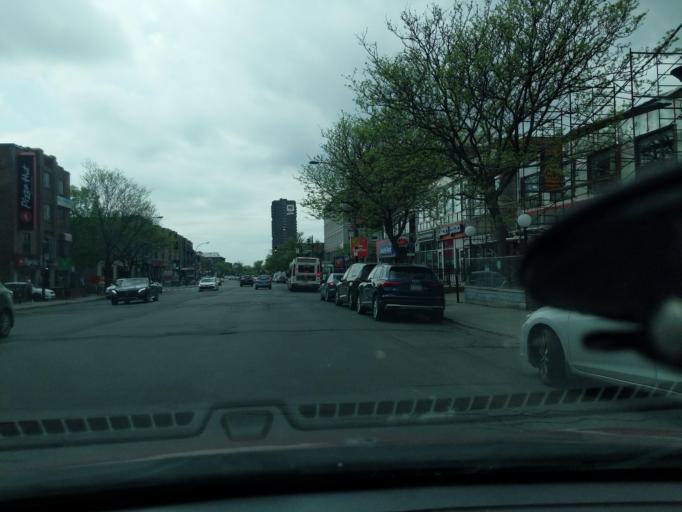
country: CA
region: Quebec
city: Saint-Raymond
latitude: 45.4860
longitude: -73.6272
